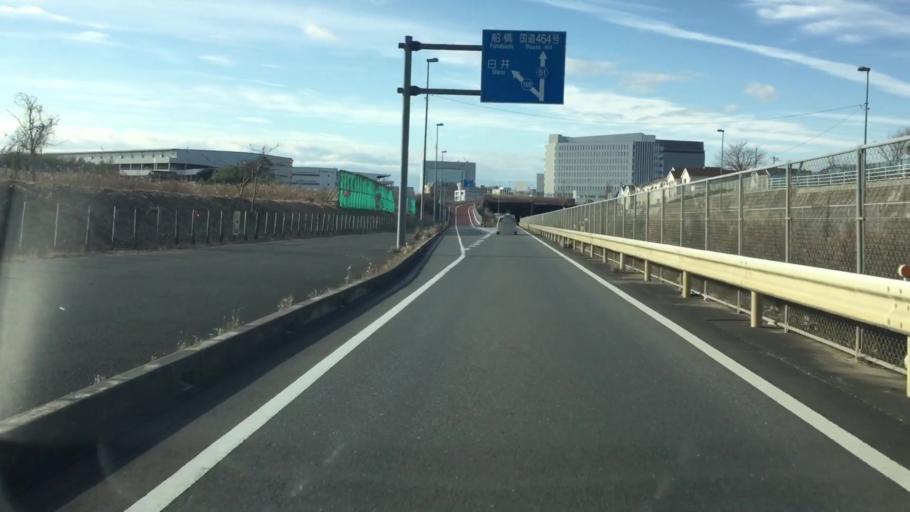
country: JP
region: Chiba
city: Shiroi
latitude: 35.8145
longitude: 140.1274
